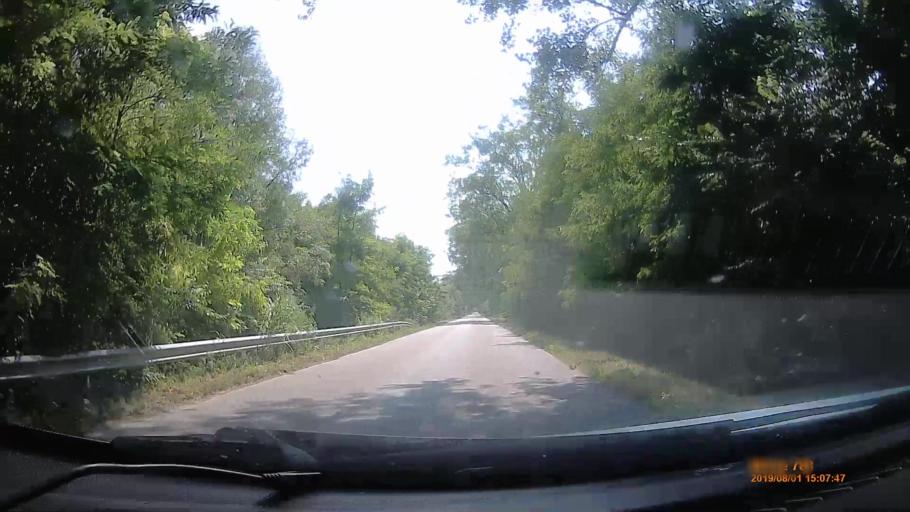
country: HU
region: Baranya
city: Sellye
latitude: 45.8562
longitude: 17.8256
